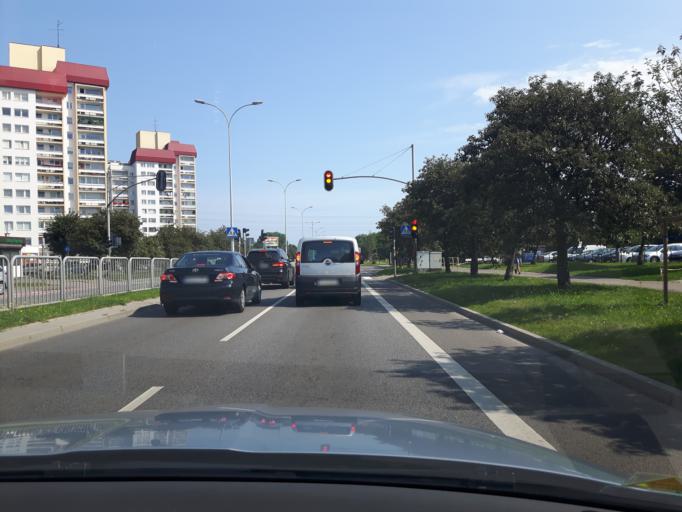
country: PL
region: Pomeranian Voivodeship
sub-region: Gdansk
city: Gdansk
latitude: 54.4033
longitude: 18.6114
